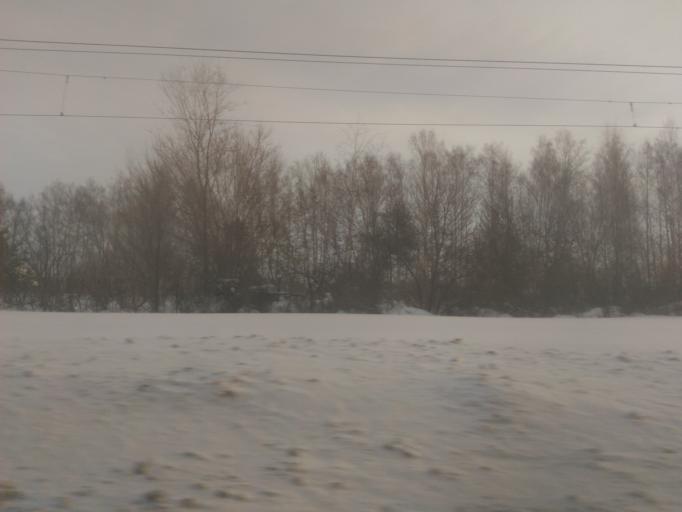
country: RU
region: Ulyanovsk
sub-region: Ulyanovskiy Rayon
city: Ulyanovsk
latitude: 54.3674
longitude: 48.3194
